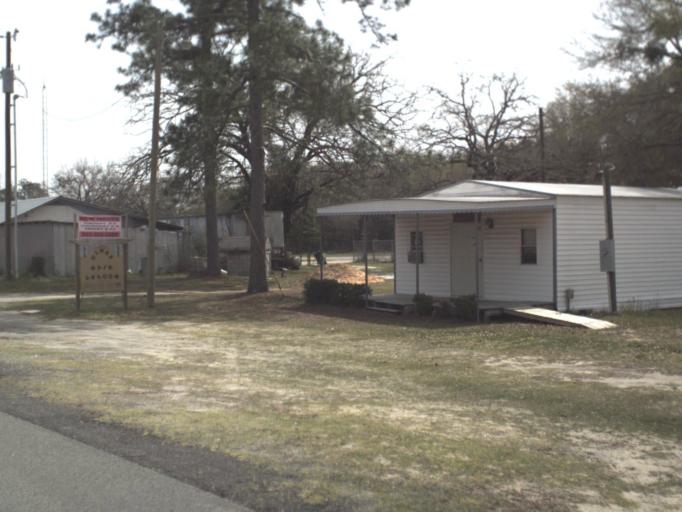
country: US
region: Alabama
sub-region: Geneva County
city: Geneva
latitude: 30.9428
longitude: -85.8209
